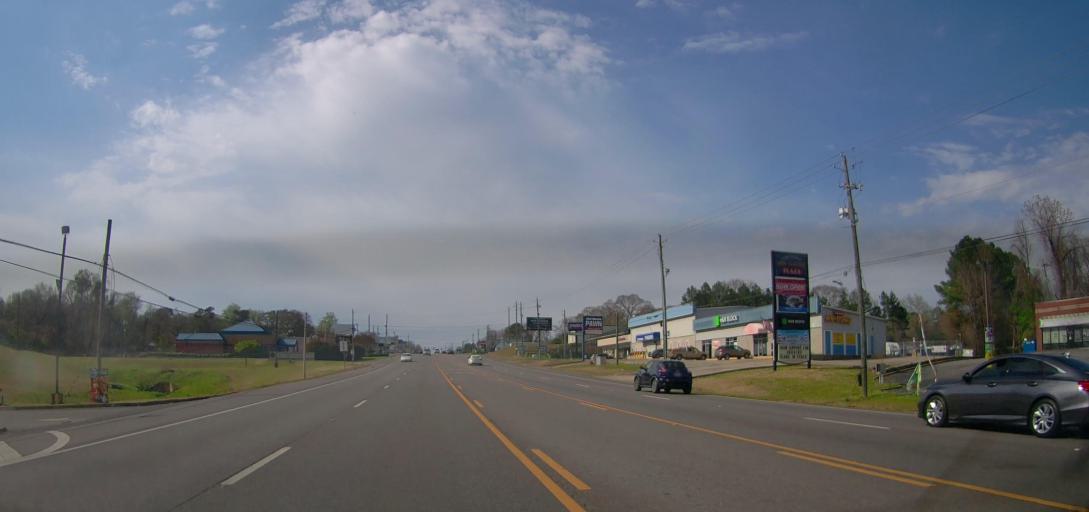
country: US
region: Alabama
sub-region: Jefferson County
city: Forestdale
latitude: 33.5637
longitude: -86.8947
